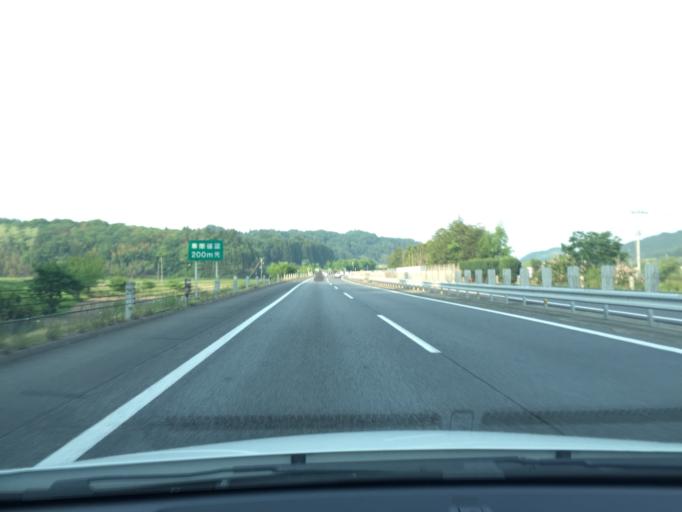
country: JP
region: Fukushima
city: Sukagawa
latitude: 37.1581
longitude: 140.2553
